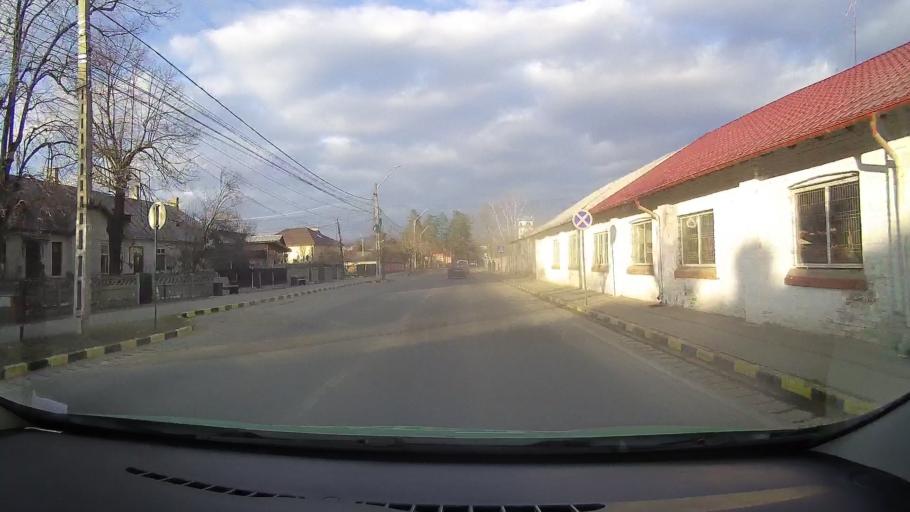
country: RO
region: Dambovita
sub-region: Municipiul Moreni
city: Moreni
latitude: 44.9808
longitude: 25.6385
